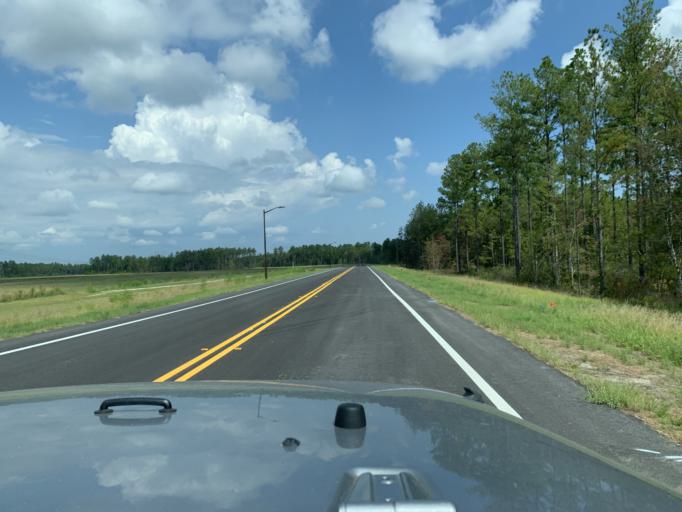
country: US
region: Georgia
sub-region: Chatham County
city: Bloomingdale
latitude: 32.0942
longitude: -81.3568
